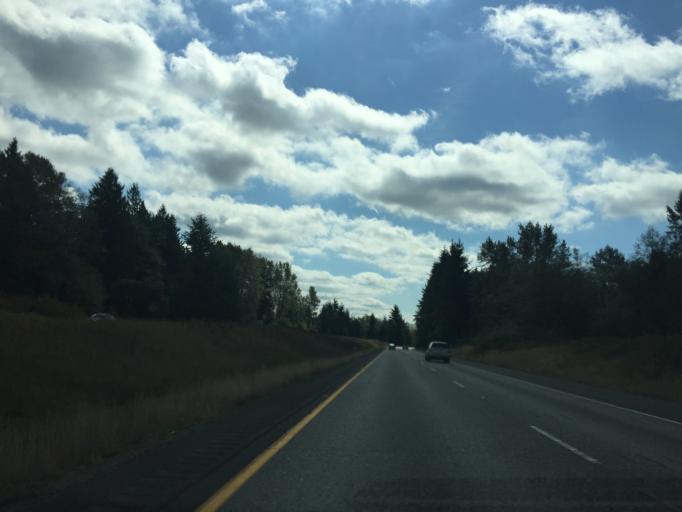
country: US
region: Washington
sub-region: Skagit County
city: Burlington
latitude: 48.5528
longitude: -122.3505
